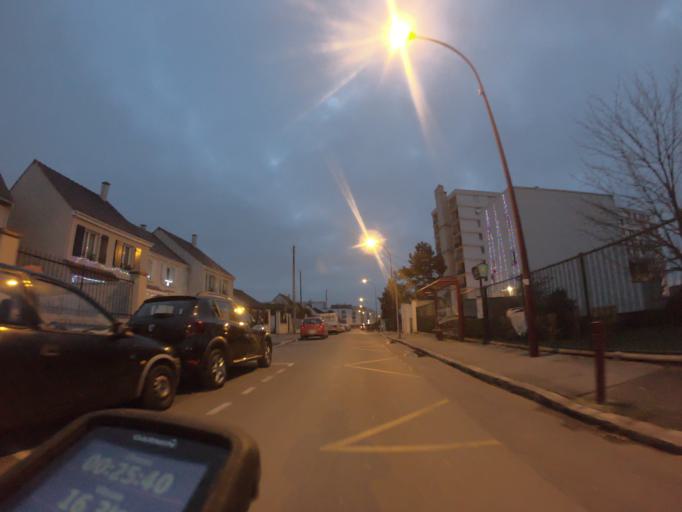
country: FR
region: Ile-de-France
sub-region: Departement du Val-de-Marne
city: Fresnes
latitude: 48.7648
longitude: 2.3295
